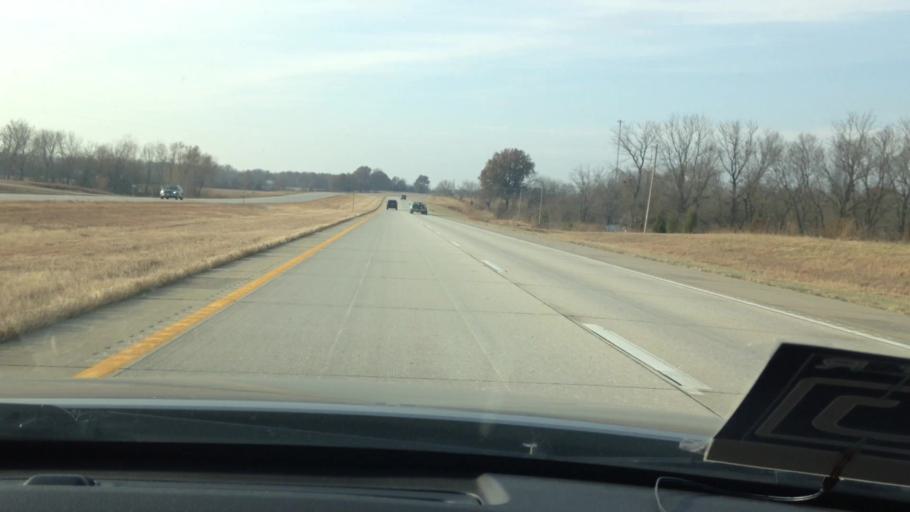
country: US
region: Missouri
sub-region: Henry County
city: Clinton
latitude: 38.4390
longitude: -93.9449
